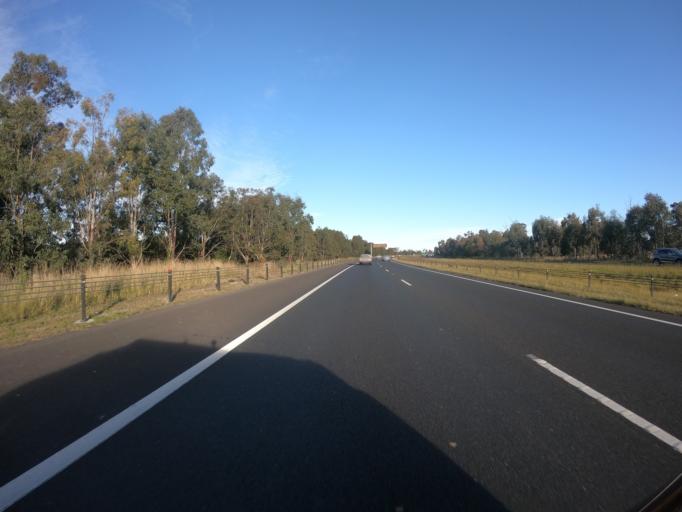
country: AU
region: New South Wales
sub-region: Blacktown
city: Doonside
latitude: -33.7786
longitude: 150.8575
